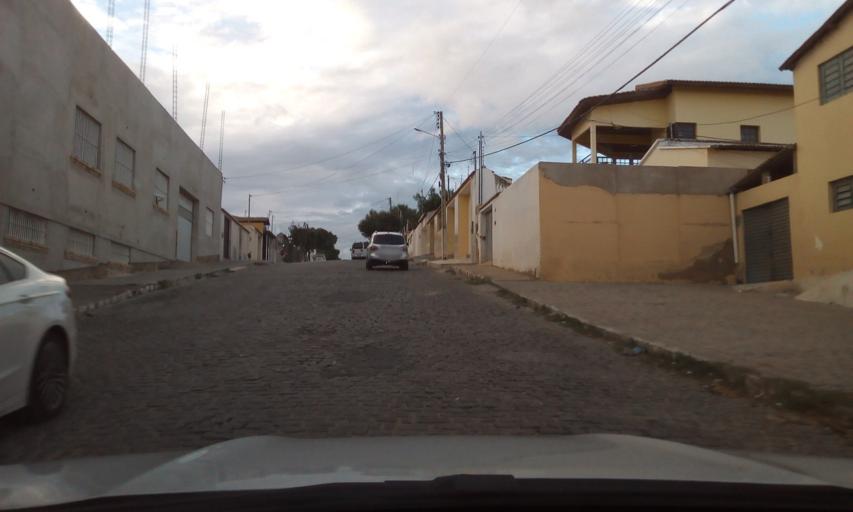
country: BR
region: Paraiba
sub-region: Picui
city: Picui
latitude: -6.5088
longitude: -36.3416
